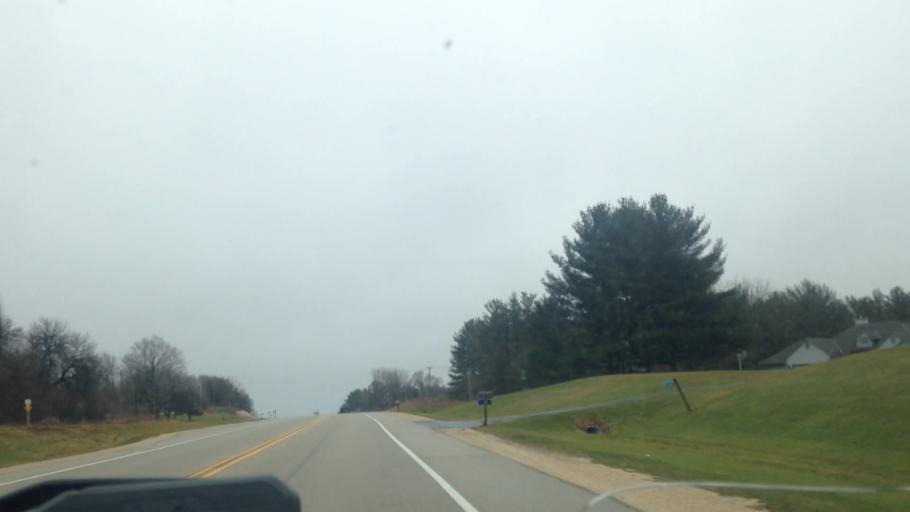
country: US
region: Wisconsin
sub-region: Dodge County
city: Horicon
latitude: 43.4736
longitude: -88.5981
